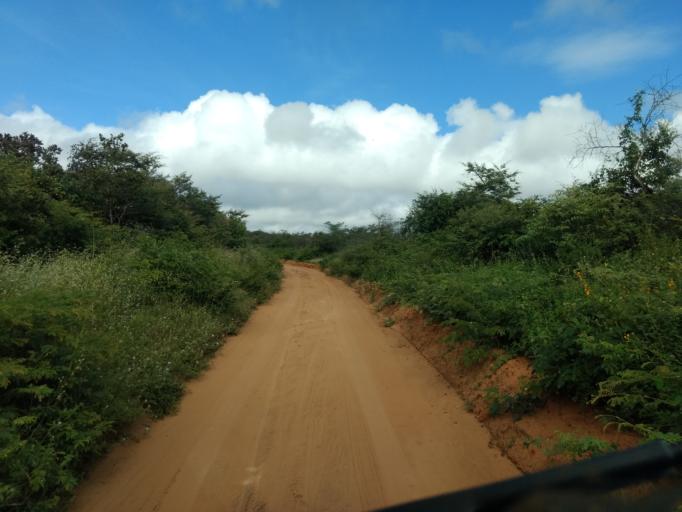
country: BR
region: Ceara
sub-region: Crateus
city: Crateus
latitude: -5.2105
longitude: -40.9422
